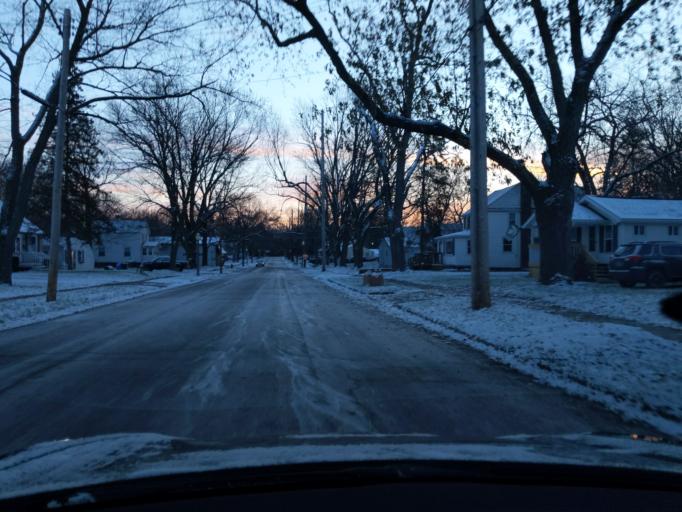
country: US
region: Michigan
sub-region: Ingham County
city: Lansing
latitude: 42.7003
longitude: -84.5566
